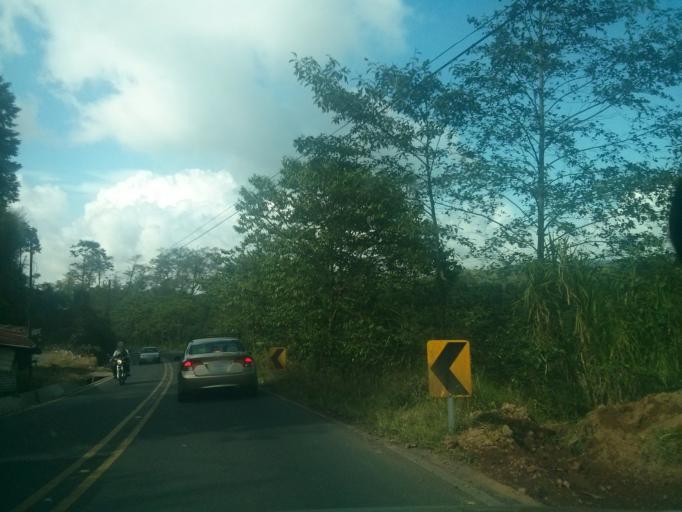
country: CR
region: Heredia
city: Santo Domingo
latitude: 10.1810
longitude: -84.1556
